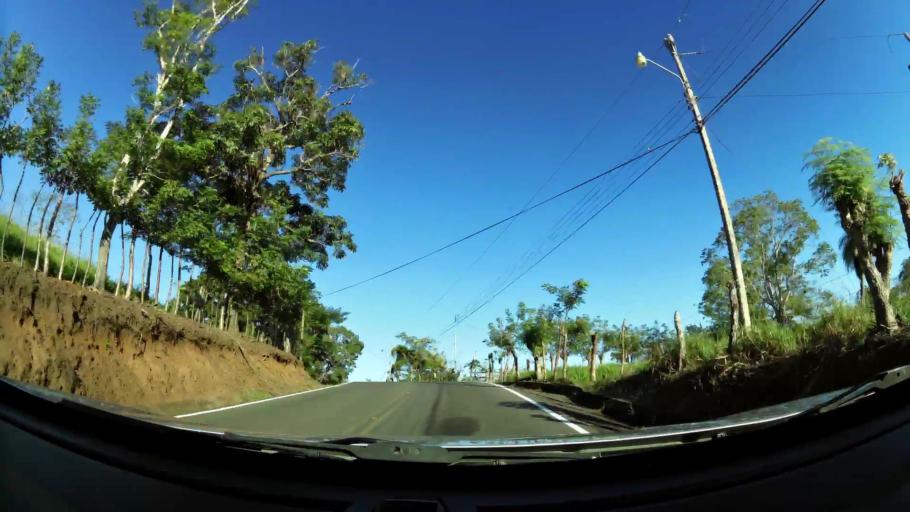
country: CR
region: Puntarenas
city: Miramar
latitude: 10.1417
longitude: -84.8455
